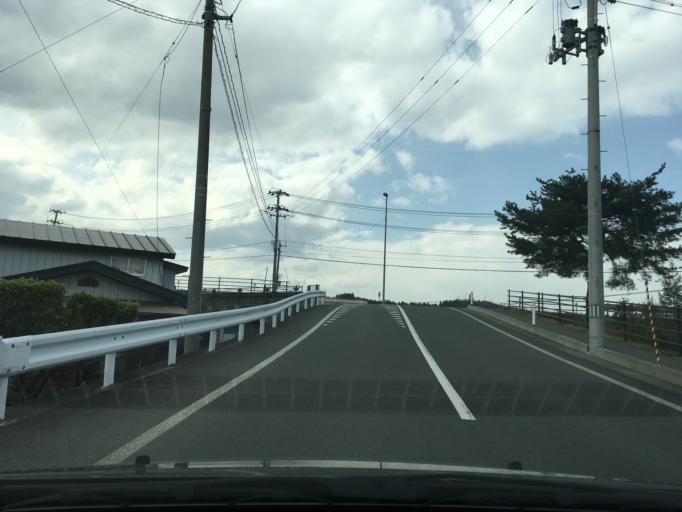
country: JP
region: Iwate
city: Mizusawa
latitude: 39.0588
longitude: 141.1296
